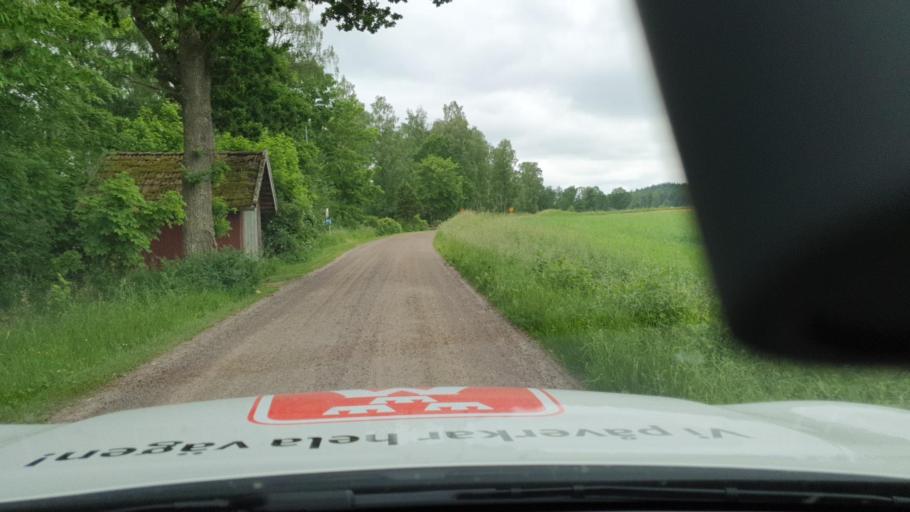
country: SE
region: Vaestra Goetaland
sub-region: Hjo Kommun
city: Hjo
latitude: 58.3532
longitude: 14.3359
